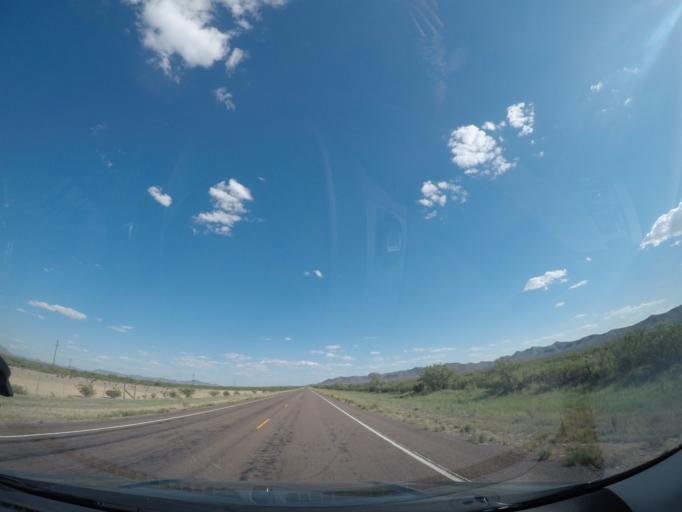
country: US
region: Texas
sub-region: Culberson County
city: Van Horn
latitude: 30.9511
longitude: -104.8135
